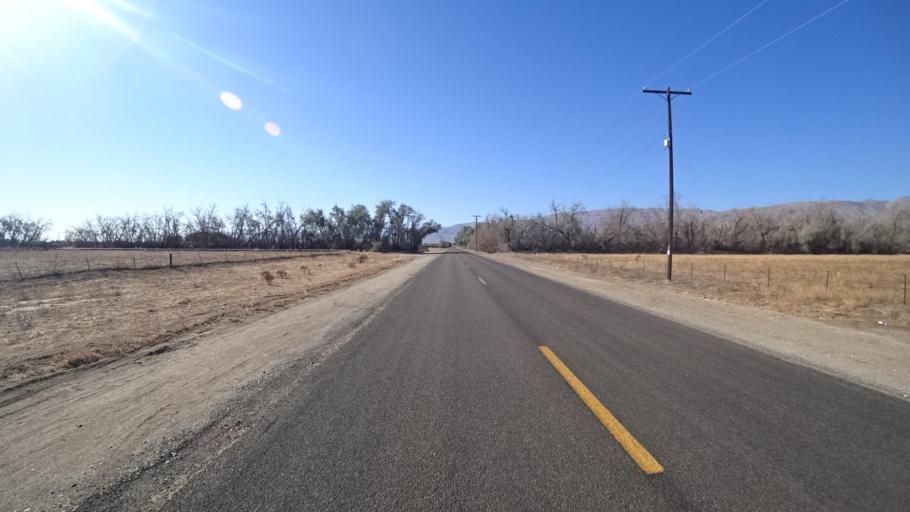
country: US
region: California
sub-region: San Diego County
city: Borrego Springs
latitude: 33.2748
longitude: -116.3750
